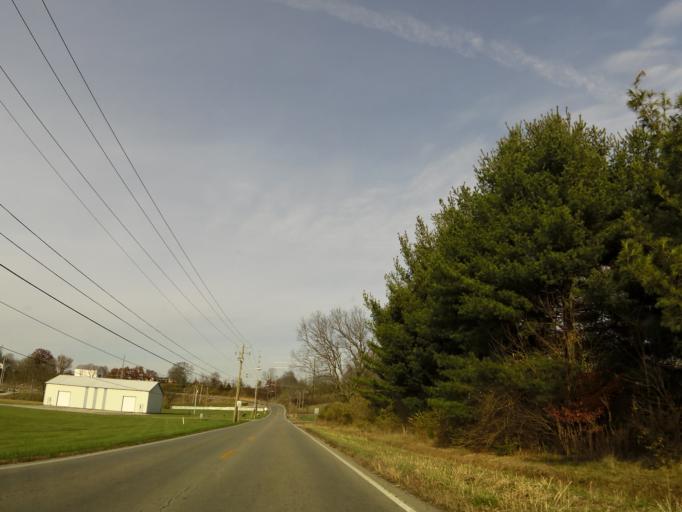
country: US
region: Kentucky
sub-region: Harrison County
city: Cynthiana
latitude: 38.3742
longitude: -84.2926
